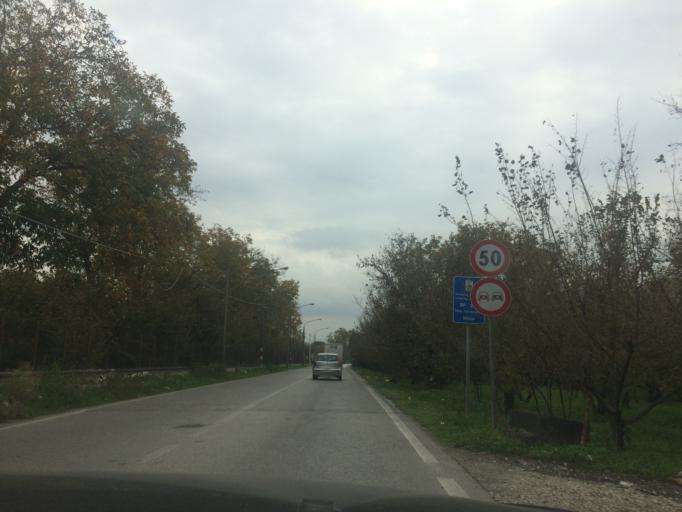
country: IT
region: Campania
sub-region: Provincia di Napoli
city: Piazzolla
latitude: 40.8936
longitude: 14.5313
